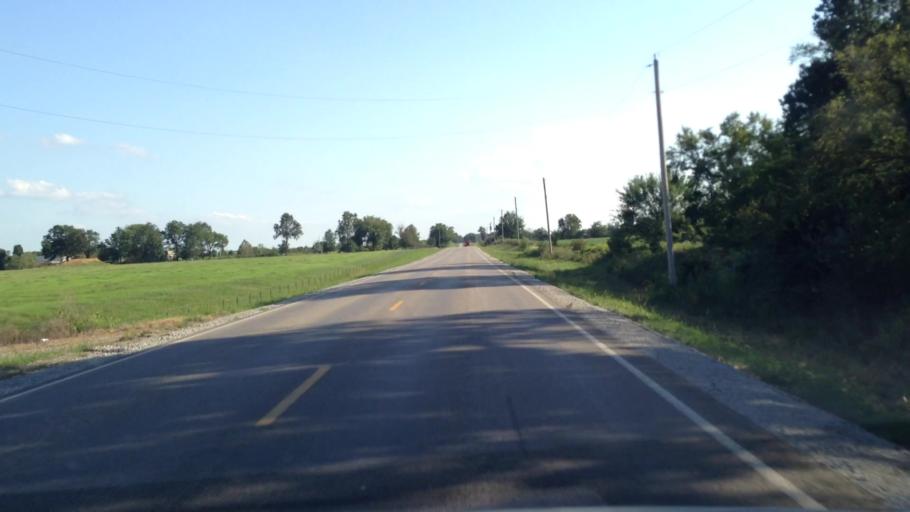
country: US
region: Kansas
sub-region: Crawford County
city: Pittsburg
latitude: 37.3494
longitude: -94.6316
